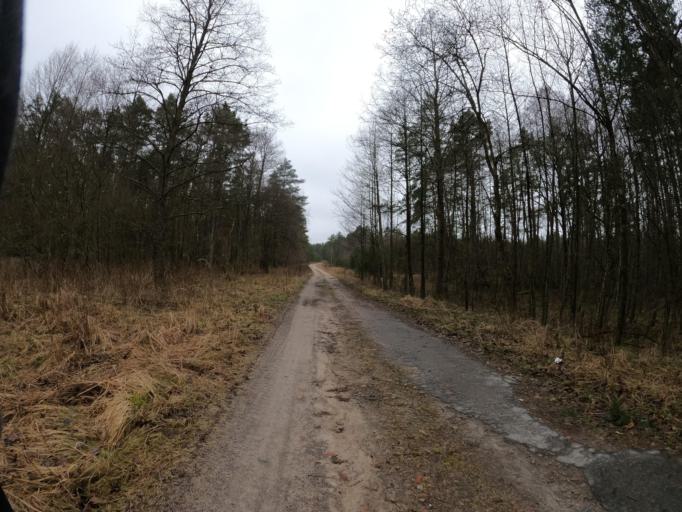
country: PL
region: Greater Poland Voivodeship
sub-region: Powiat zlotowski
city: Sypniewo
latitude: 53.5018
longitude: 16.5608
